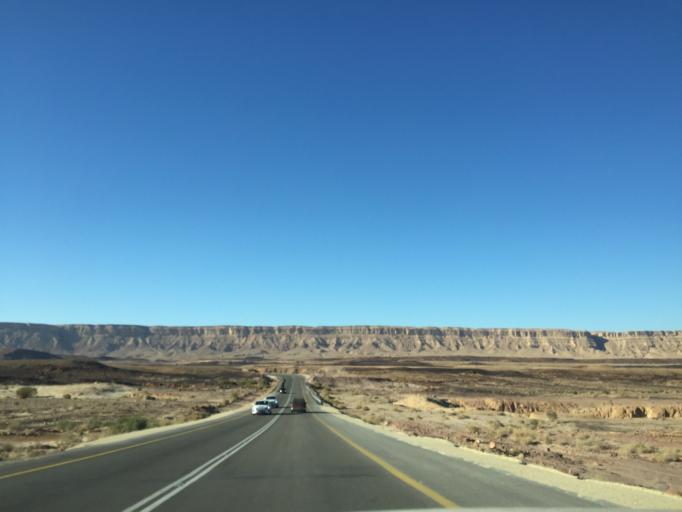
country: IL
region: Southern District
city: Mitzpe Ramon
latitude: 30.6093
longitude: 34.8627
